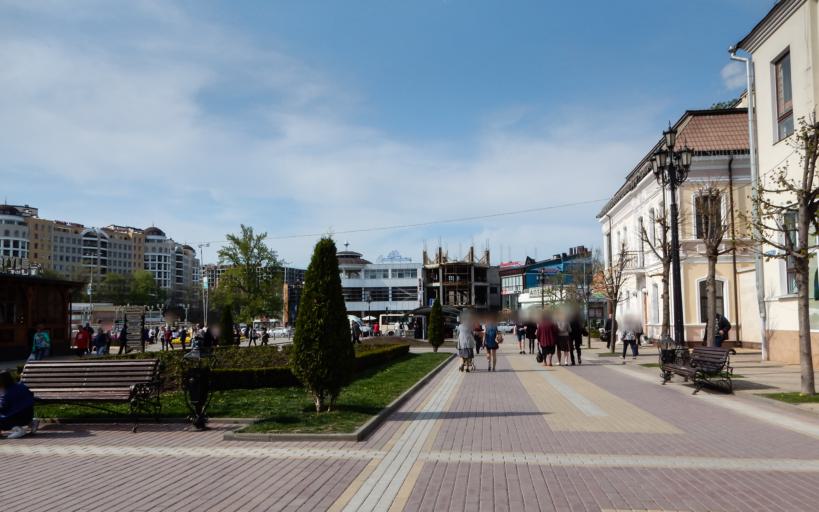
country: RU
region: Stavropol'skiy
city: Kislovodsk
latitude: 43.9045
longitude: 42.7169
